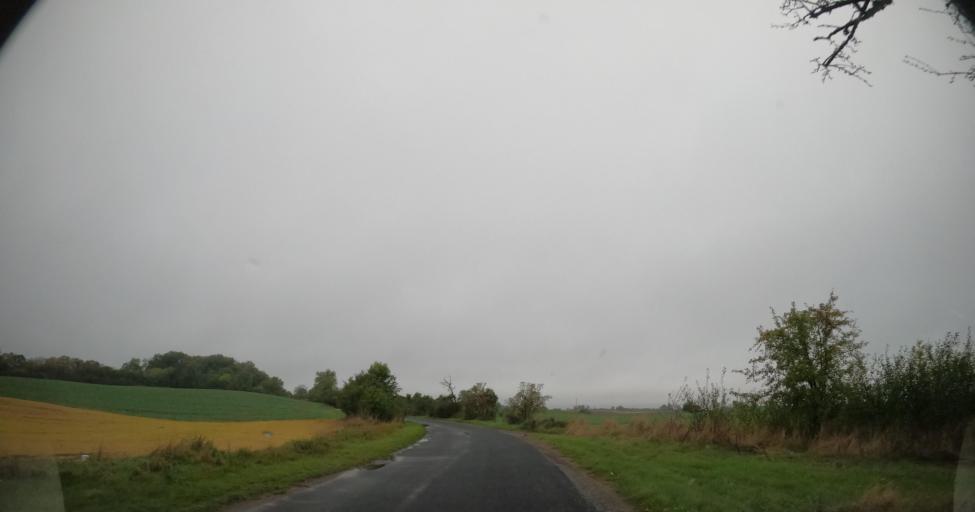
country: PL
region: West Pomeranian Voivodeship
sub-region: Powiat gryfinski
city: Banie
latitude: 53.0564
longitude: 14.7156
